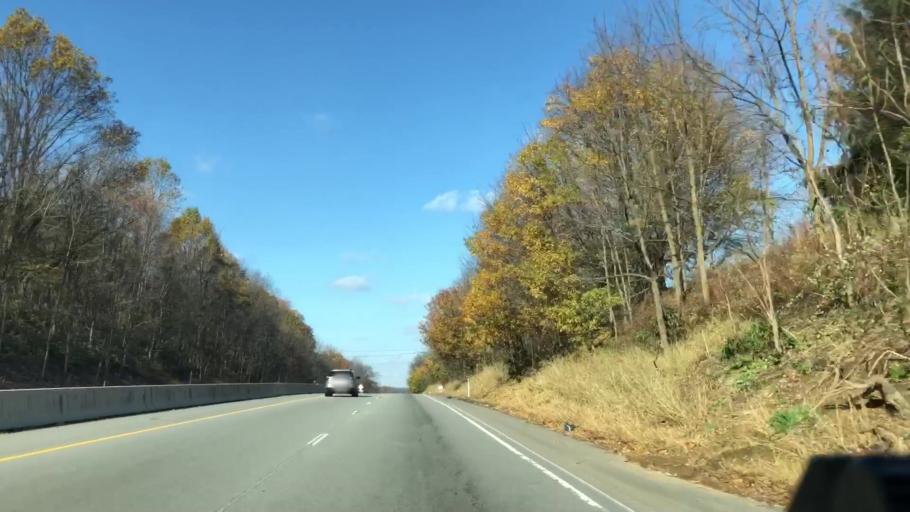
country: US
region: Pennsylvania
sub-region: Montgomery County
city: Halfway House
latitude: 40.3004
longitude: -75.6364
